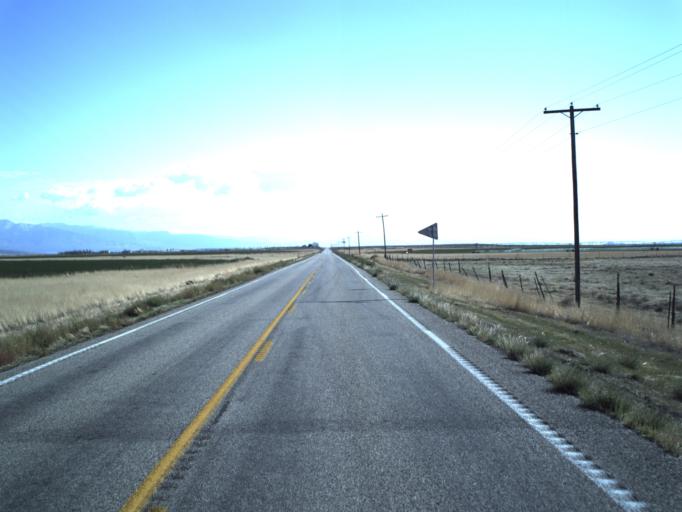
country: US
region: Utah
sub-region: Millard County
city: Delta
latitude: 39.1972
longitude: -112.4100
